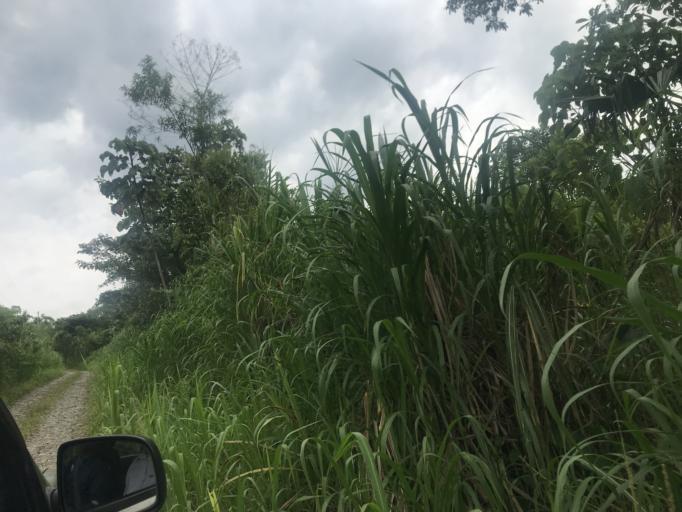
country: EC
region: Napo
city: Tena
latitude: -1.0252
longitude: -77.7422
